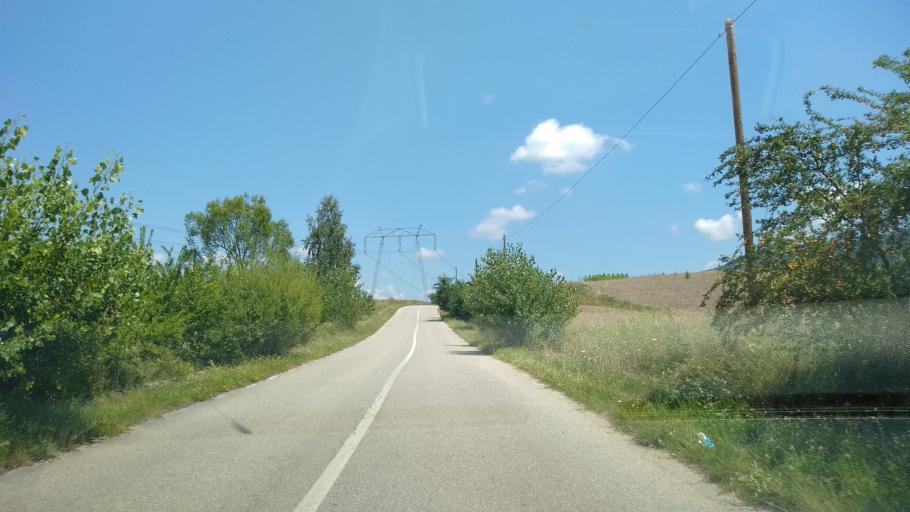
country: RO
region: Hunedoara
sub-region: Comuna Santamaria-Orlea
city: Santamaria-Orlea
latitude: 45.5888
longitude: 22.9943
